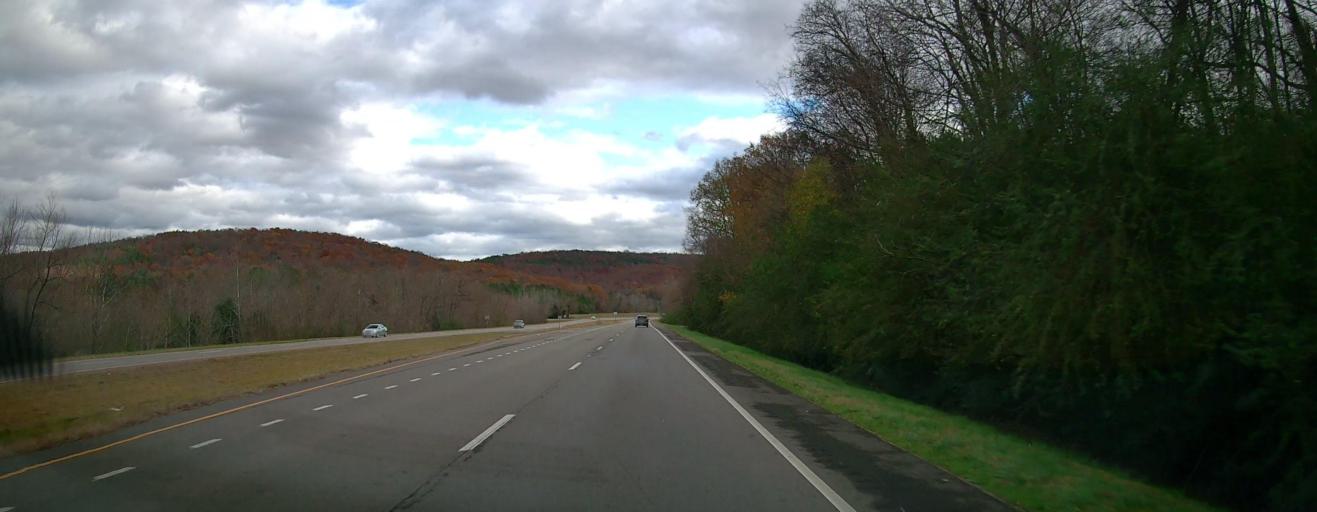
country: US
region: Alabama
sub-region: Morgan County
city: Falkville
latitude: 34.3309
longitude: -87.0096
